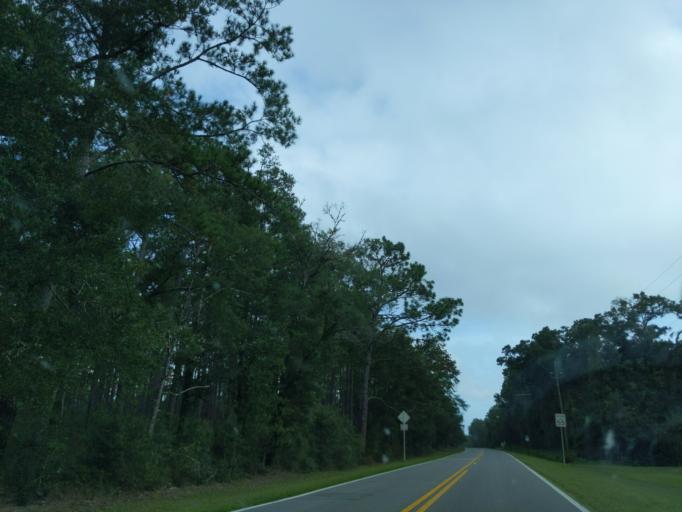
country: US
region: Florida
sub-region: Wakulla County
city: Crawfordville
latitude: 30.1202
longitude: -84.3147
